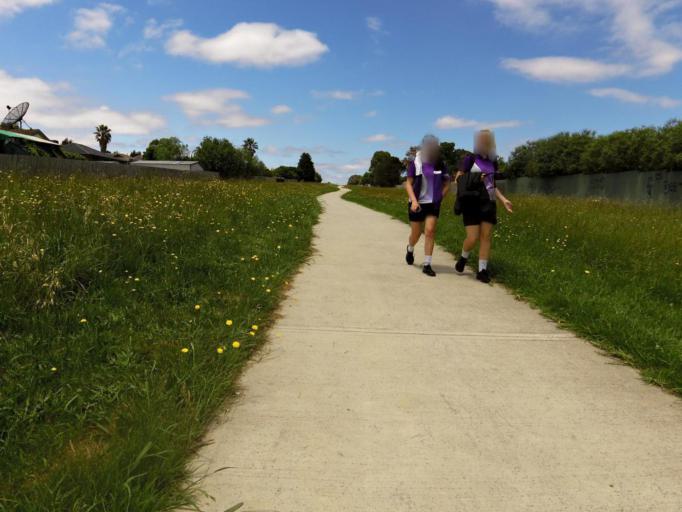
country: AU
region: Victoria
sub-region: Casey
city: Endeavour Hills
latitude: -37.9700
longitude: 145.2686
